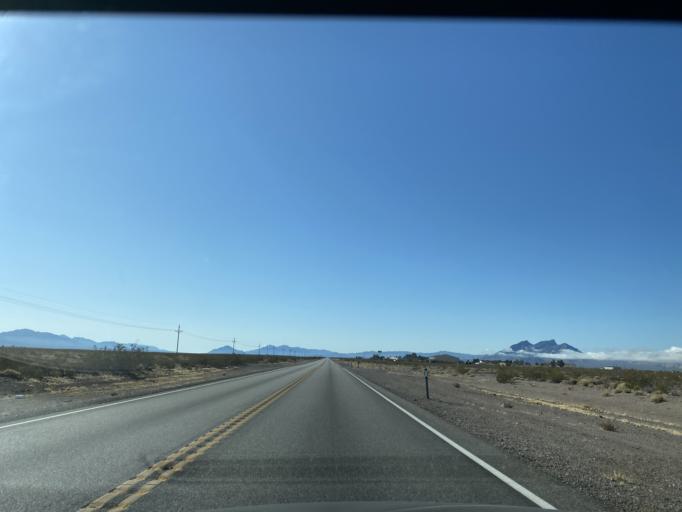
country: US
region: Nevada
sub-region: Nye County
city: Pahrump
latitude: 36.5028
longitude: -116.4213
